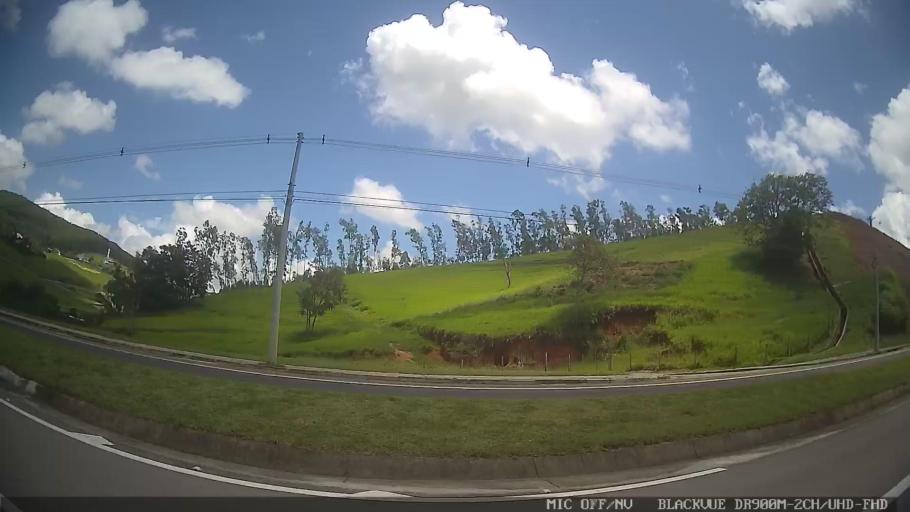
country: BR
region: Sao Paulo
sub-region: Caraguatatuba
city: Caraguatatuba
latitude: -23.4532
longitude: -45.5972
